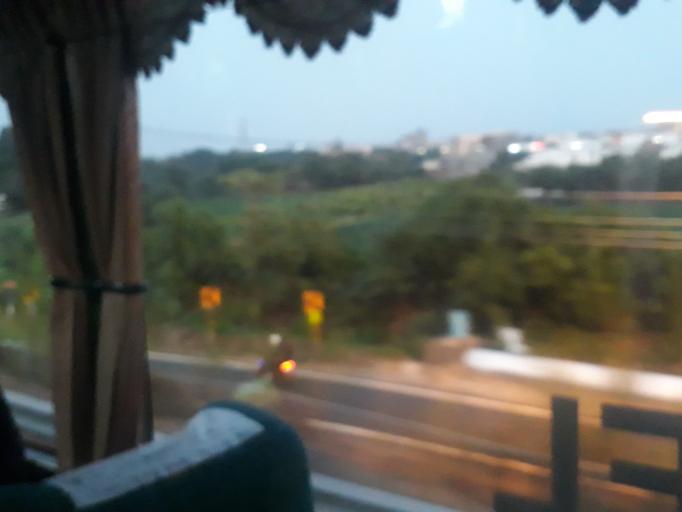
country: TW
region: Taiwan
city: Xinying
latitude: 23.3092
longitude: 120.2926
